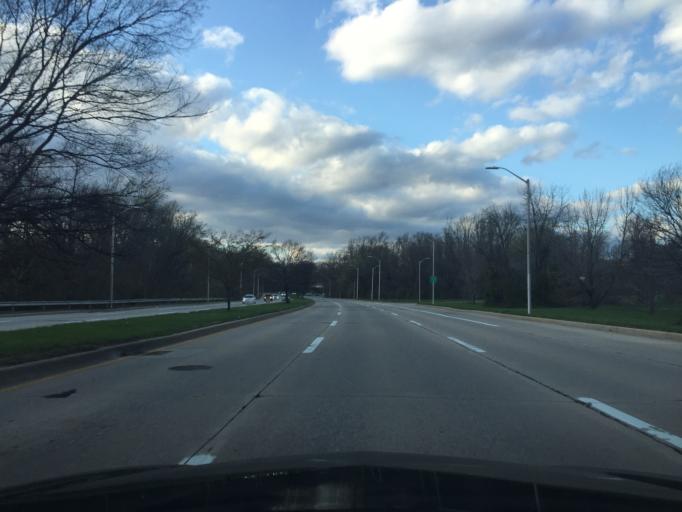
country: US
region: Maryland
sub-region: Baltimore County
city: Parkville
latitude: 39.3641
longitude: -76.5732
